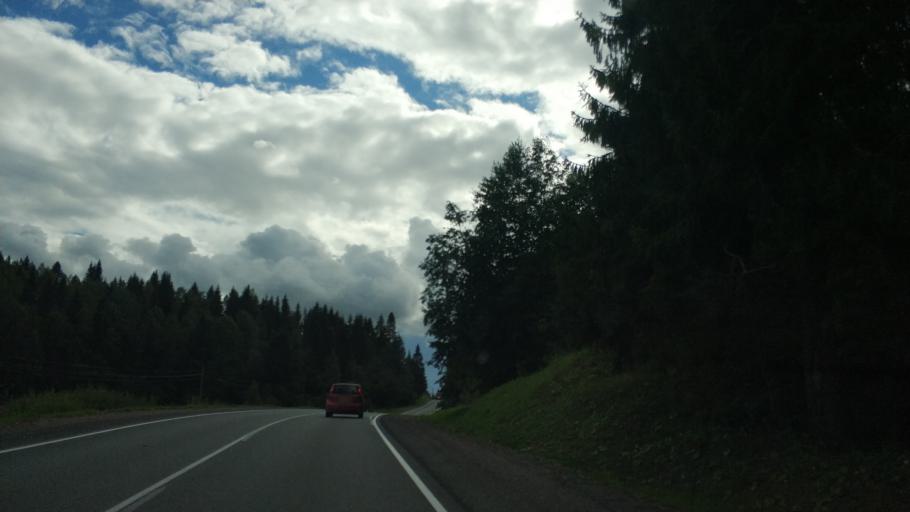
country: RU
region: Republic of Karelia
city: Khelyulya
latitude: 61.7715
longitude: 30.6551
